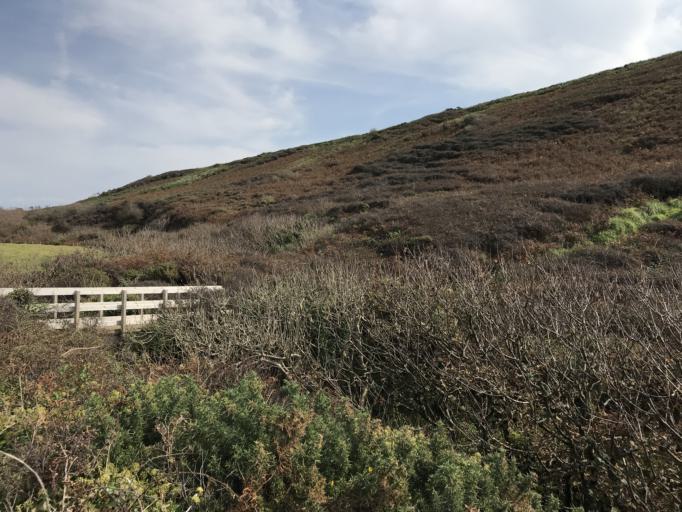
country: GB
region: England
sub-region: Cornwall
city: Flexbury
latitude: 51.0124
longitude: -4.5245
